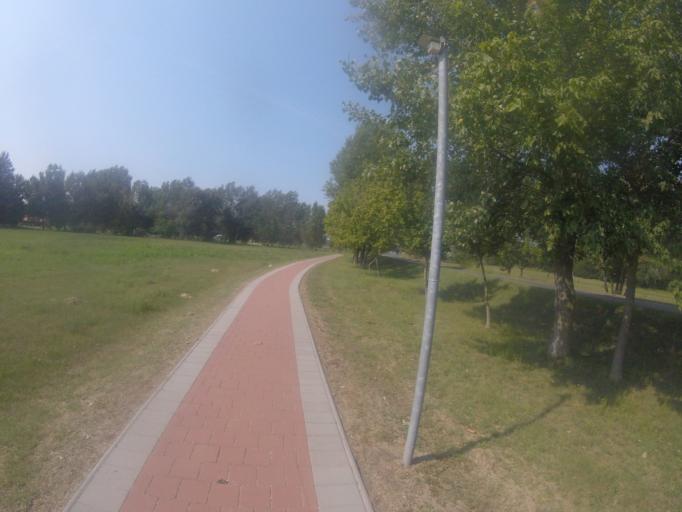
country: HU
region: Bacs-Kiskun
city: Ersekcsanad
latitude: 46.2524
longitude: 18.9740
